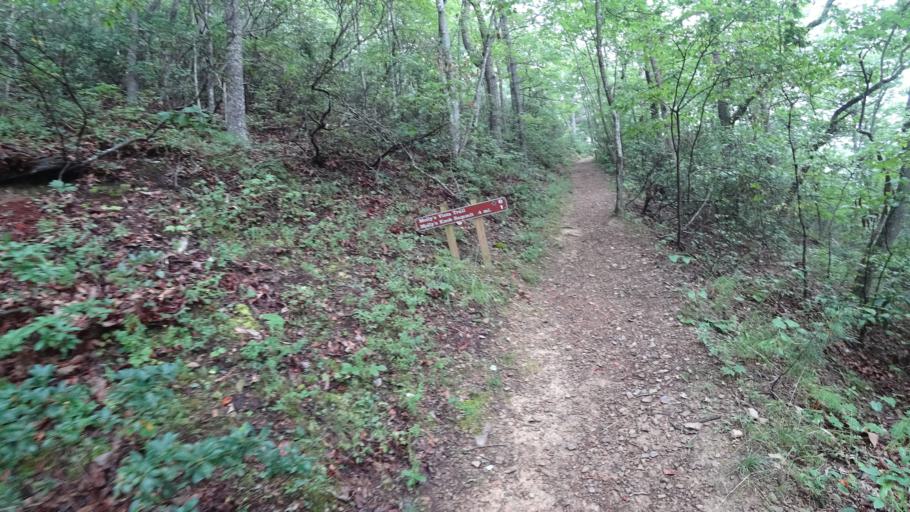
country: US
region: Virginia
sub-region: Smyth County
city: Marion
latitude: 36.8824
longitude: -81.5094
